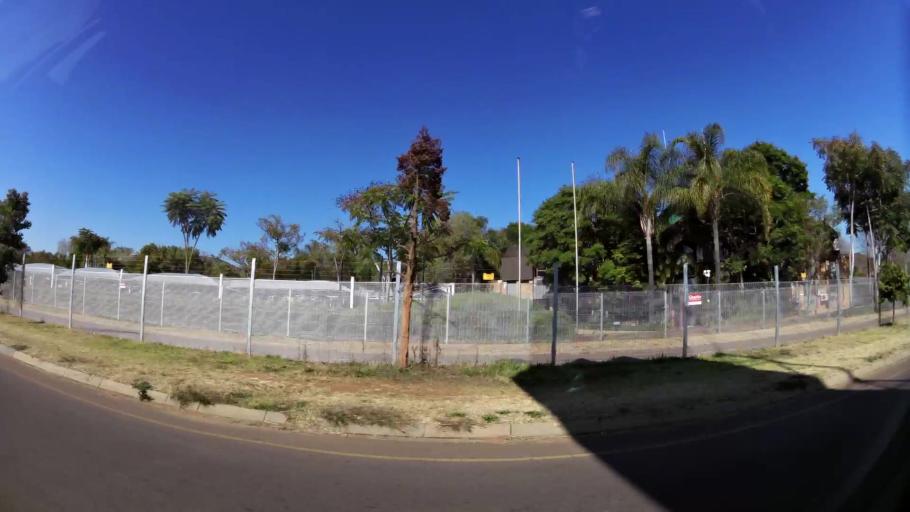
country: ZA
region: Gauteng
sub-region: City of Tshwane Metropolitan Municipality
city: Pretoria
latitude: -25.7711
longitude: 28.2127
